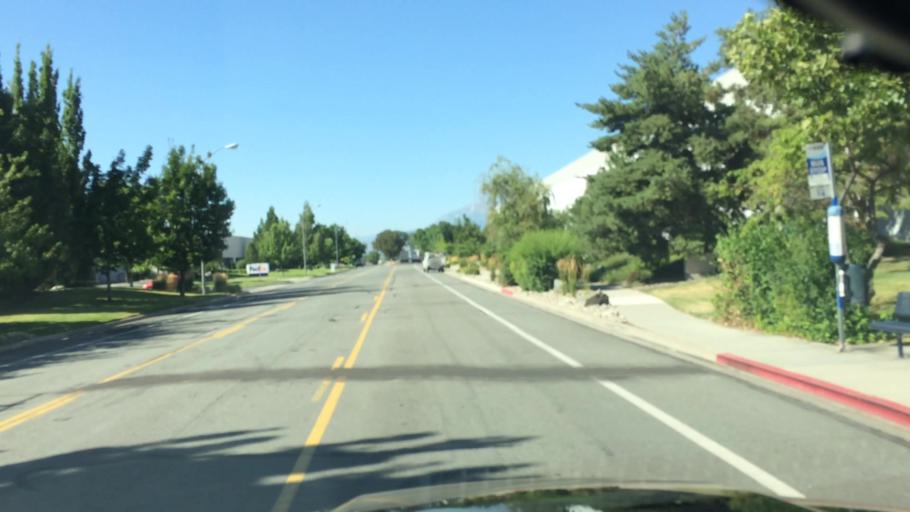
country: US
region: Nevada
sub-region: Washoe County
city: Sparks
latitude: 39.5030
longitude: -119.7541
